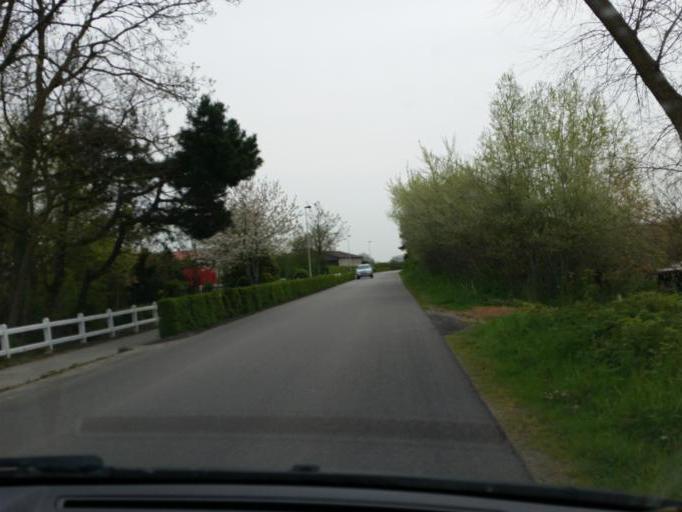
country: NL
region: Zeeland
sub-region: Gemeente Sluis
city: Sluis
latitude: 51.3450
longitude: 3.3369
